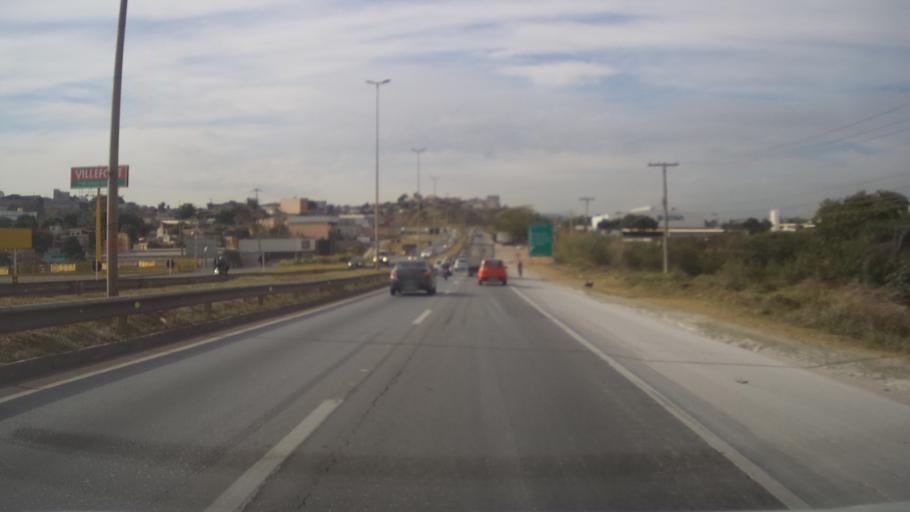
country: BR
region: Minas Gerais
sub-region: Contagem
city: Contagem
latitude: -19.9143
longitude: -44.0403
